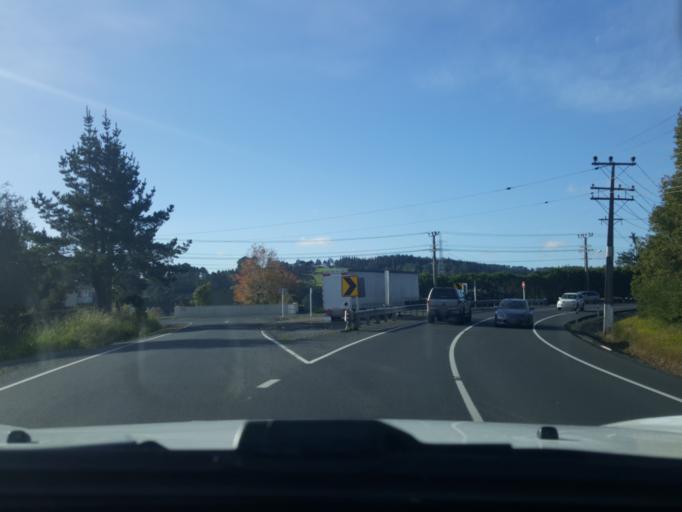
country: NZ
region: Auckland
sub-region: Auckland
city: Muriwai Beach
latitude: -36.7629
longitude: 174.5770
